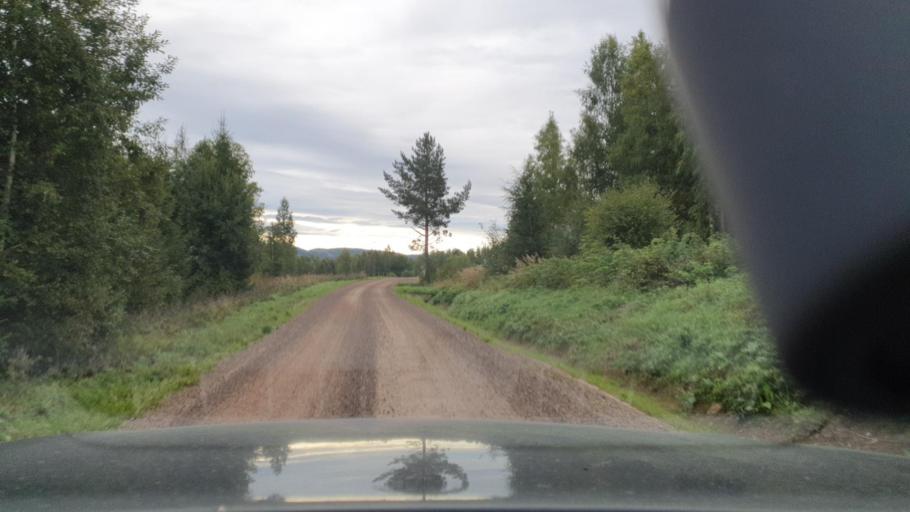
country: SE
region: Vaermland
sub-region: Torsby Kommun
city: Torsby
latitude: 59.9736
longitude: 12.8592
